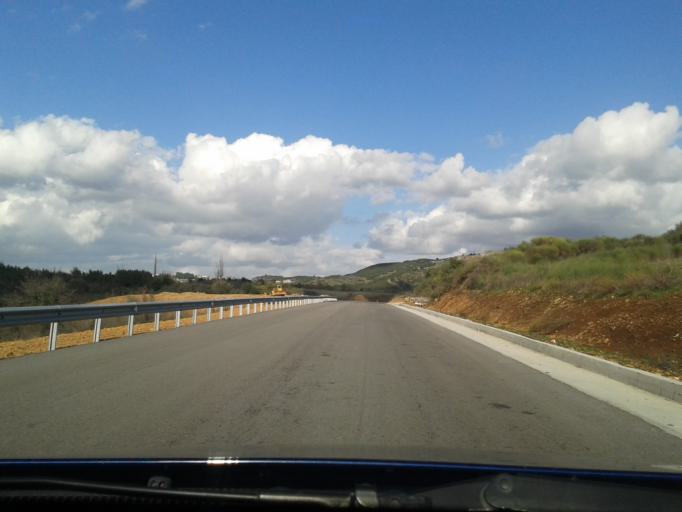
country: GR
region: West Greece
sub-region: Nomos Aitolias kai Akarnanias
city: Fitiai
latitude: 38.6827
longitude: 21.1674
